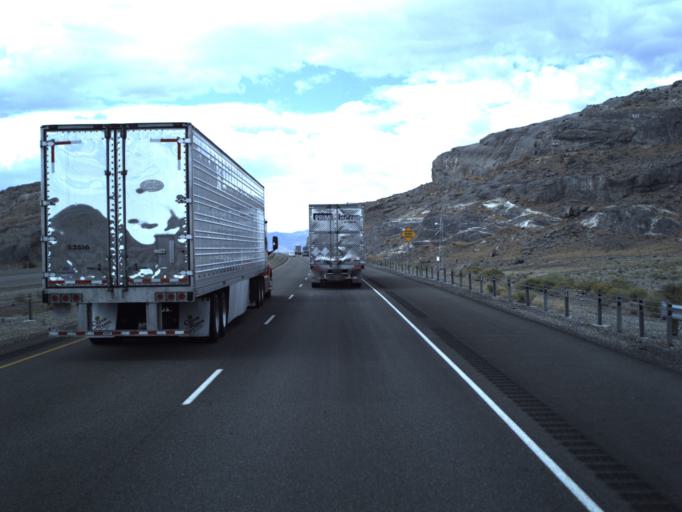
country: US
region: Utah
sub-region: Tooele County
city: Wendover
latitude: 40.7452
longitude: -114.0212
